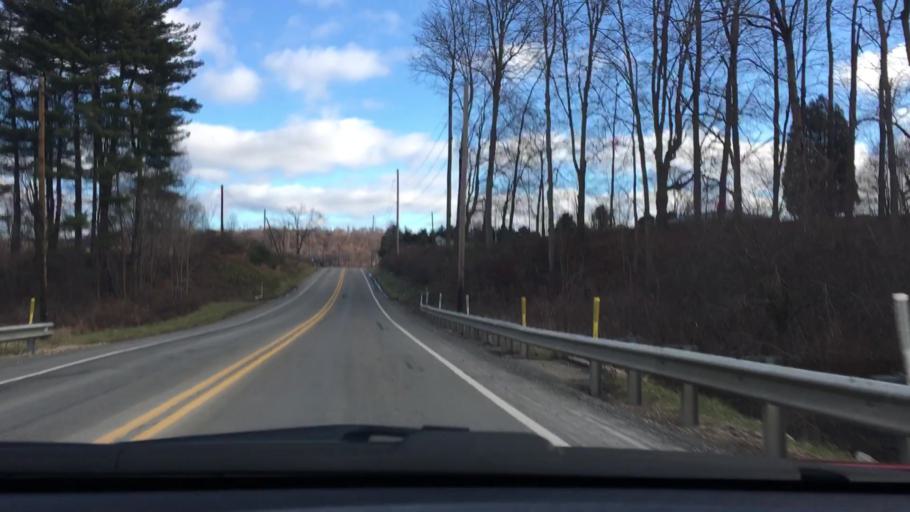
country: US
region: Pennsylvania
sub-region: Indiana County
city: Indiana
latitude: 40.6526
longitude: -79.3165
